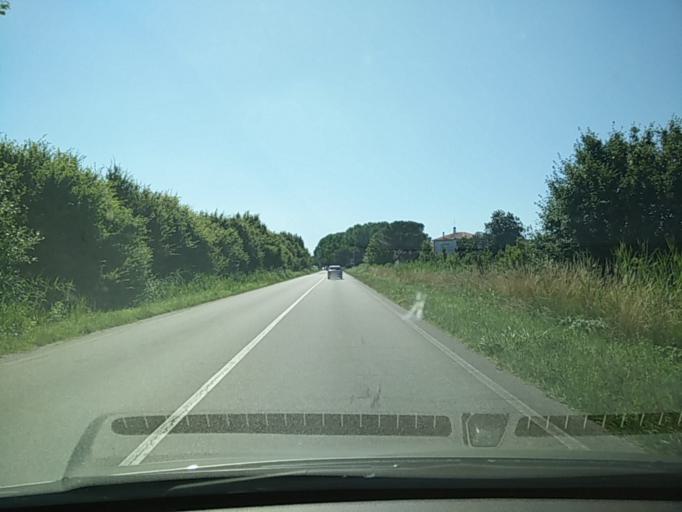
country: IT
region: Veneto
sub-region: Provincia di Venezia
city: San Giorgio di Livenza
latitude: 45.6306
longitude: 12.7775
